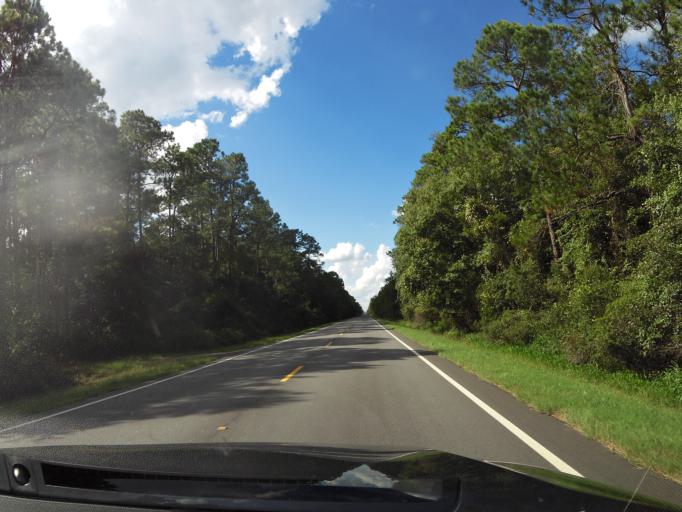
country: US
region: Georgia
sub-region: Echols County
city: Statenville
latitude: 30.7232
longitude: -83.0751
